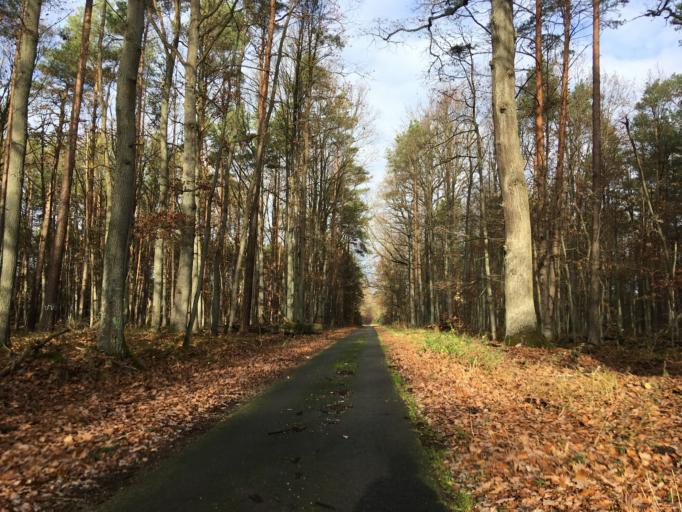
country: DE
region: Brandenburg
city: Tauer
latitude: 51.9274
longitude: 14.5116
